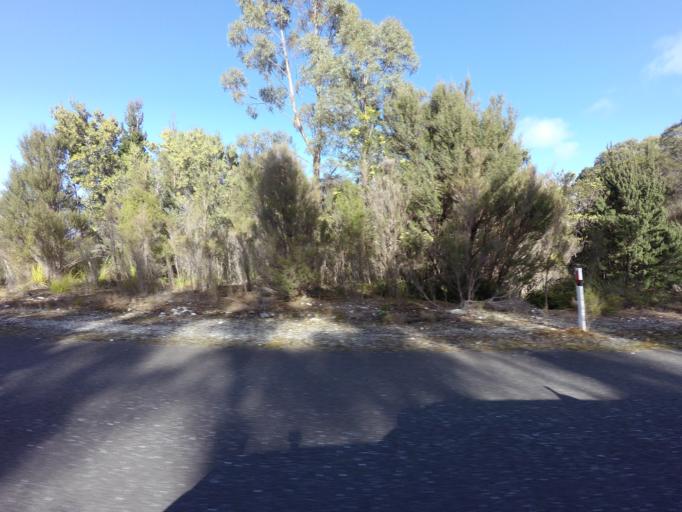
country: AU
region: Tasmania
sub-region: West Coast
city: Queenstown
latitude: -42.7714
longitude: 146.0572
